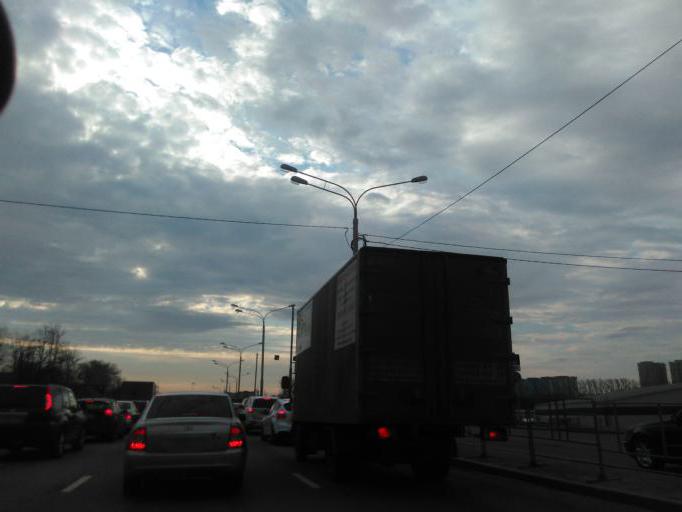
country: RU
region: Moscow
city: Pokrovskoye-Streshnevo
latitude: 55.8225
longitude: 37.4415
